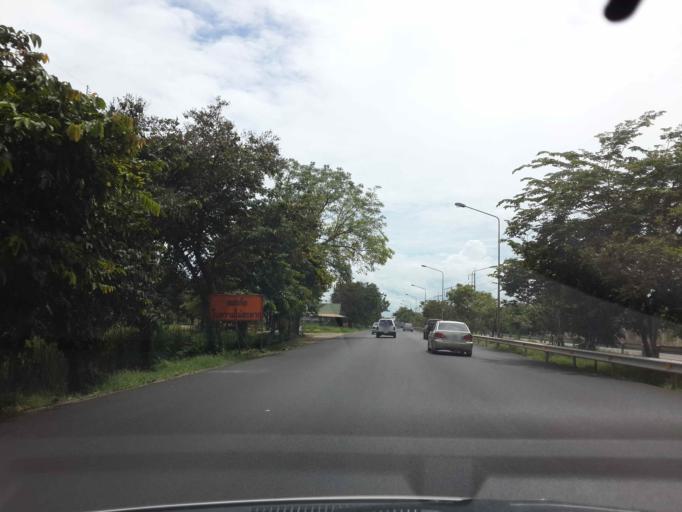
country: TH
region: Ratchaburi
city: Pak Tho
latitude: 13.4411
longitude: 99.8038
